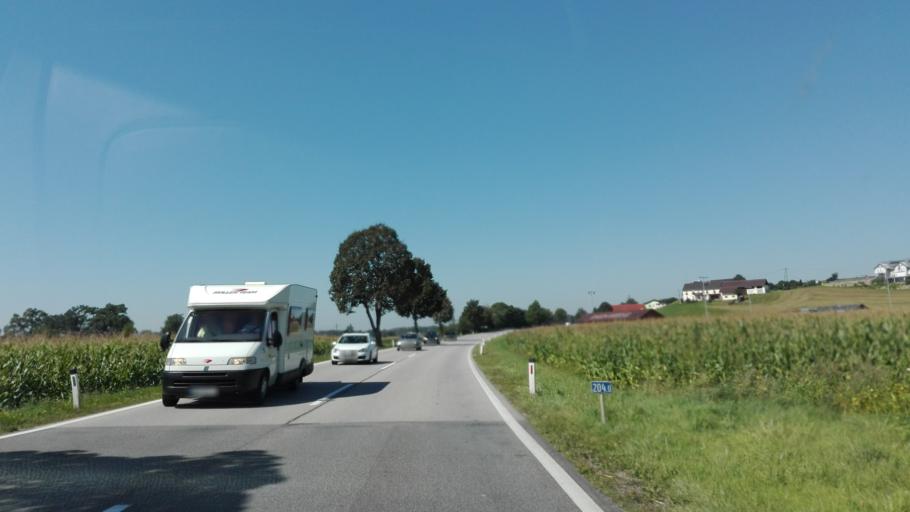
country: AT
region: Upper Austria
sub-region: Politischer Bezirk Perg
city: Perg
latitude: 48.2219
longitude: 14.7114
